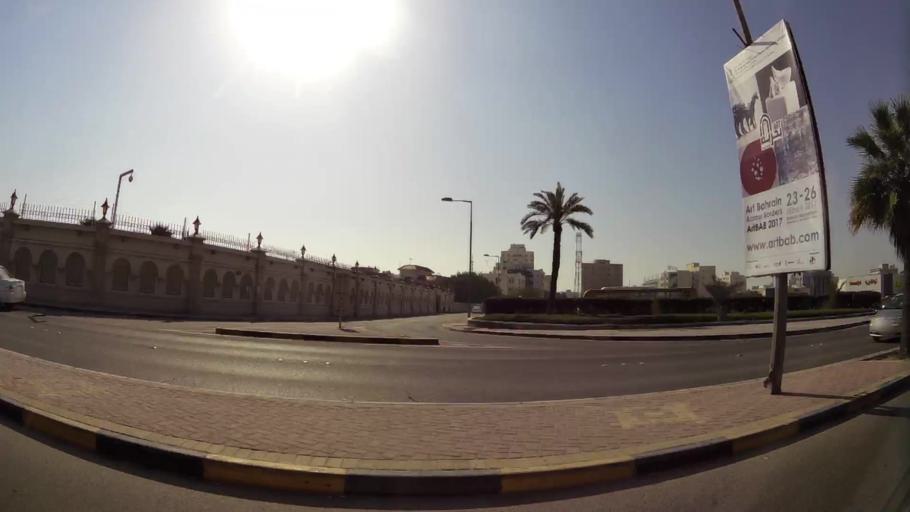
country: BH
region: Manama
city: Manama
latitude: 26.2215
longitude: 50.5863
